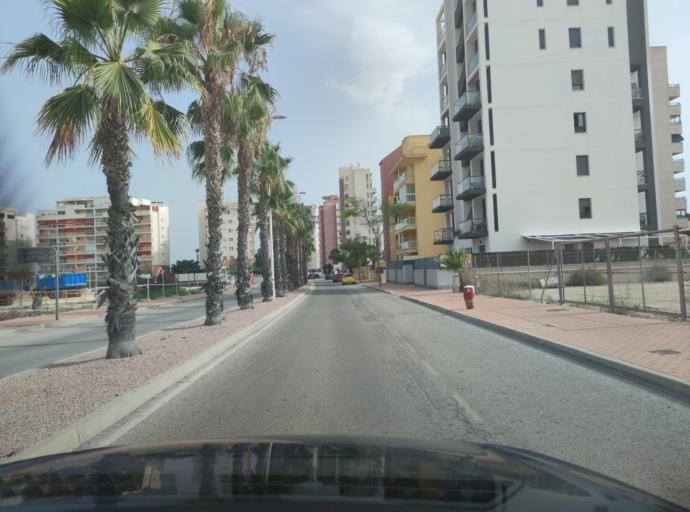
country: ES
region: Valencia
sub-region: Provincia de Alicante
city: Guardamar del Segura
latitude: 38.0987
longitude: -0.6557
